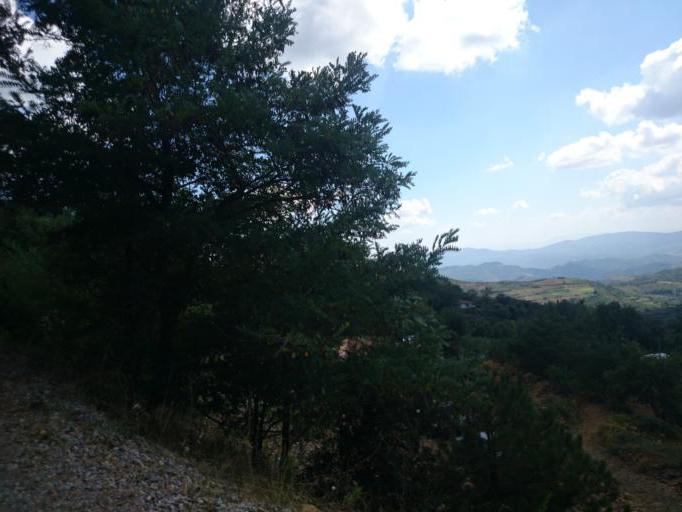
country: AL
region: Elbasan
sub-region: Rrethi i Elbasanit
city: Gjinar
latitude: 41.0337
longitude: 20.1897
